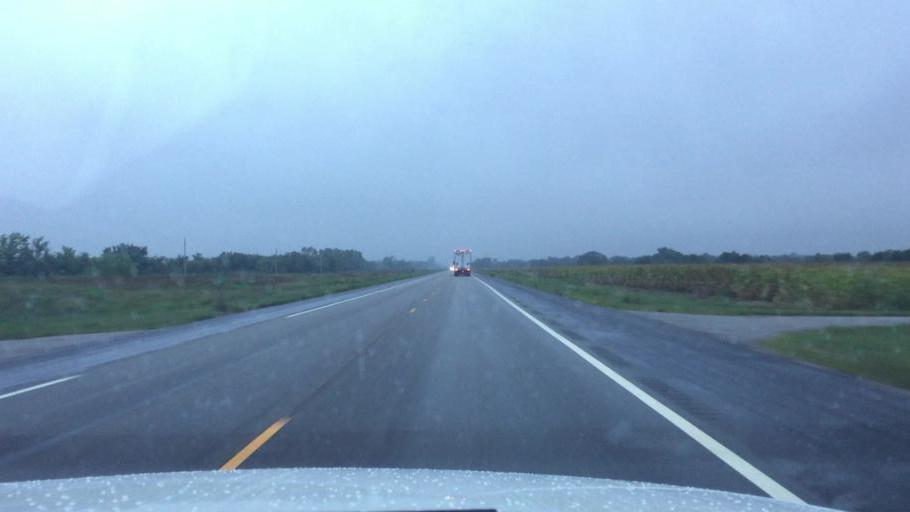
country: US
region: Kansas
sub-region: Montgomery County
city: Cherryvale
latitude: 37.4056
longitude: -95.5015
